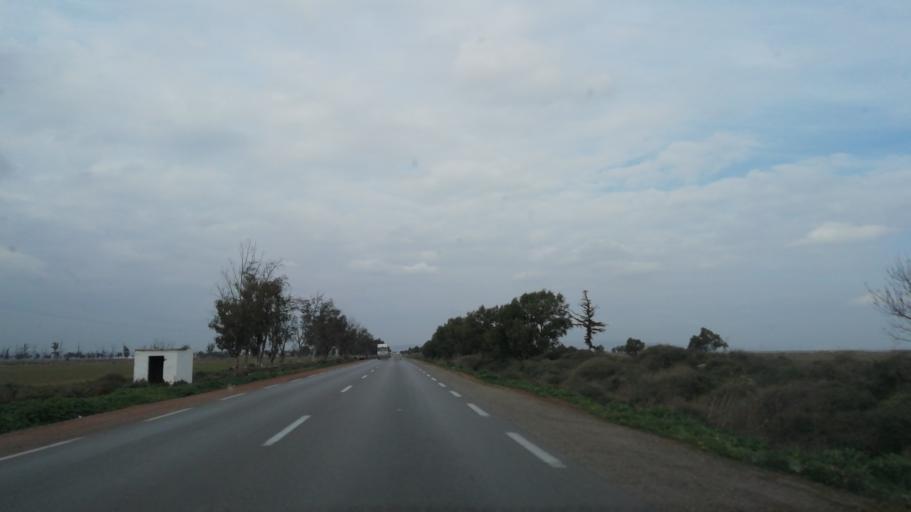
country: DZ
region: Mostaganem
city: Mostaganem
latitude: 35.6758
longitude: 0.0573
